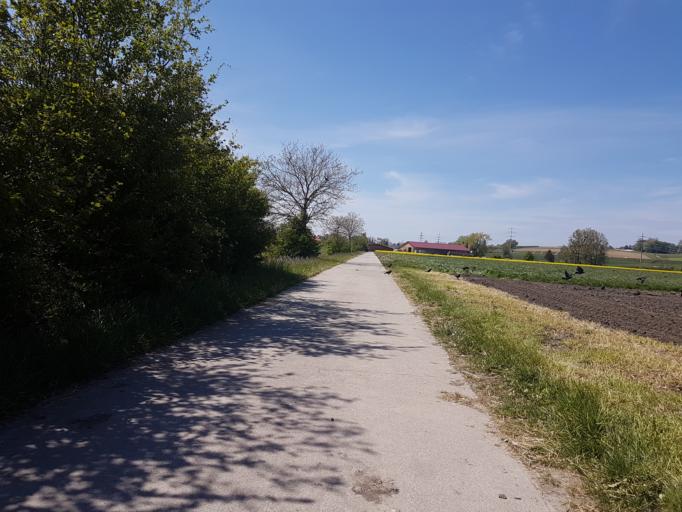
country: CH
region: Neuchatel
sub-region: Neuchatel District
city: Cornaux
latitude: 47.0307
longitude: 7.0381
